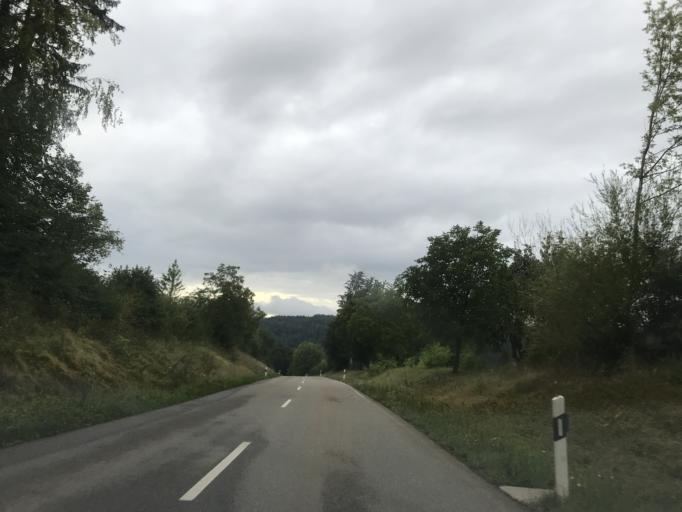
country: DE
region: Baden-Wuerttemberg
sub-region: Freiburg Region
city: Schopfheim
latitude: 47.6415
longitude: 7.8360
